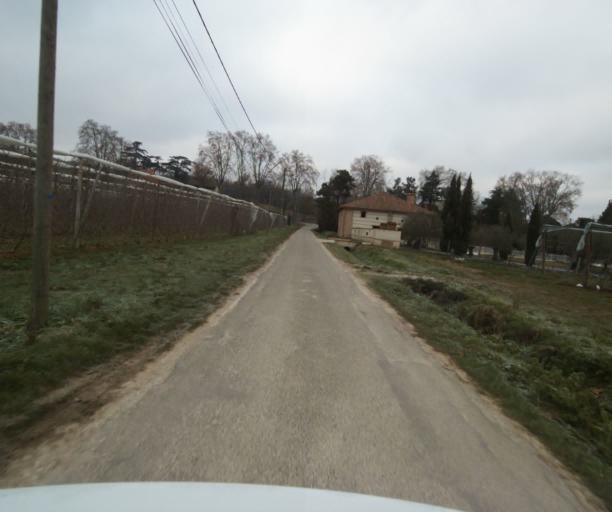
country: FR
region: Midi-Pyrenees
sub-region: Departement du Tarn-et-Garonne
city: Moissac
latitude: 44.1207
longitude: 1.1460
